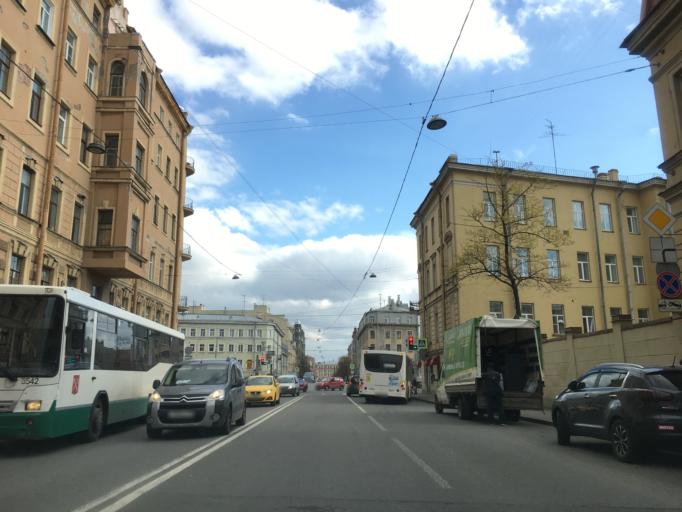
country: RU
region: St.-Petersburg
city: Admiralteisky
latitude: 59.9215
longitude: 30.2864
